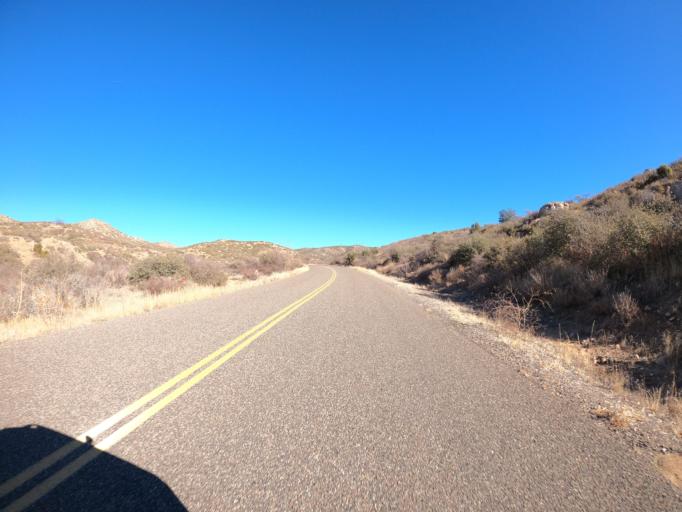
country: US
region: Arizona
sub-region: Yavapai County
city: Dewey-Humboldt
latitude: 34.5483
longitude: -112.0758
